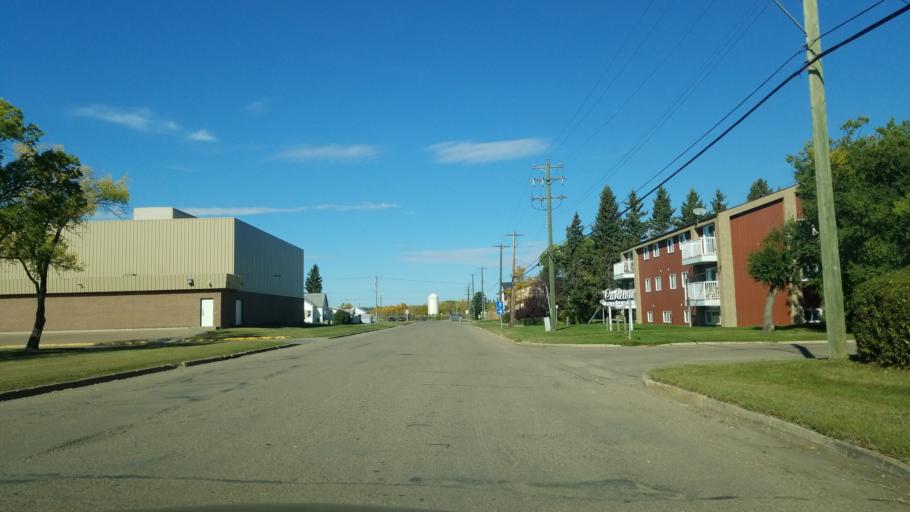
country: CA
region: Saskatchewan
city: Lloydminster
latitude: 53.2814
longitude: -109.9914
